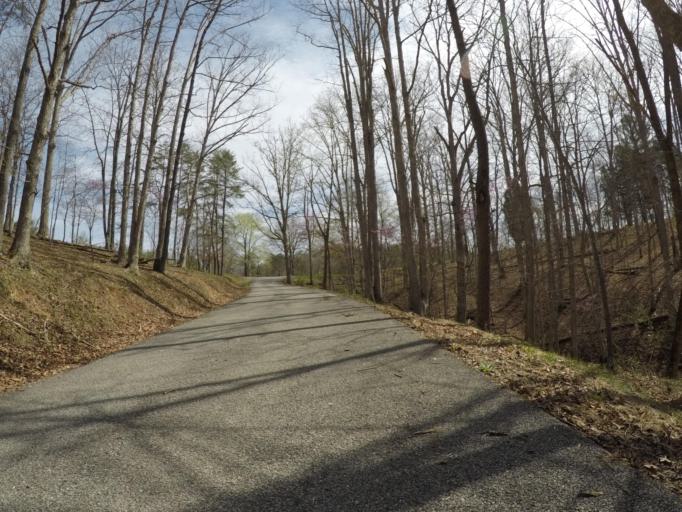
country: US
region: West Virginia
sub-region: Wayne County
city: Lavalette
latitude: 38.3093
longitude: -82.3537
